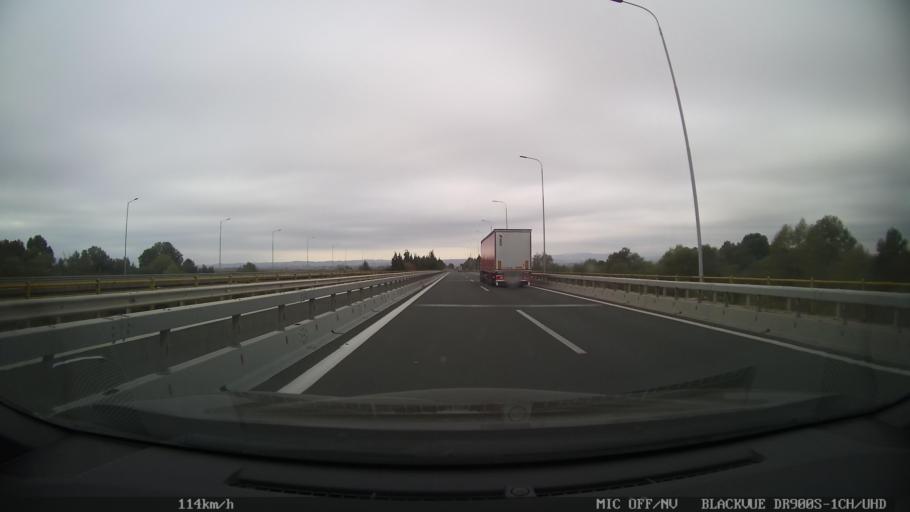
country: GR
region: Central Macedonia
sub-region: Nomos Imathias
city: Kleidi
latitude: 40.5414
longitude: 22.5853
